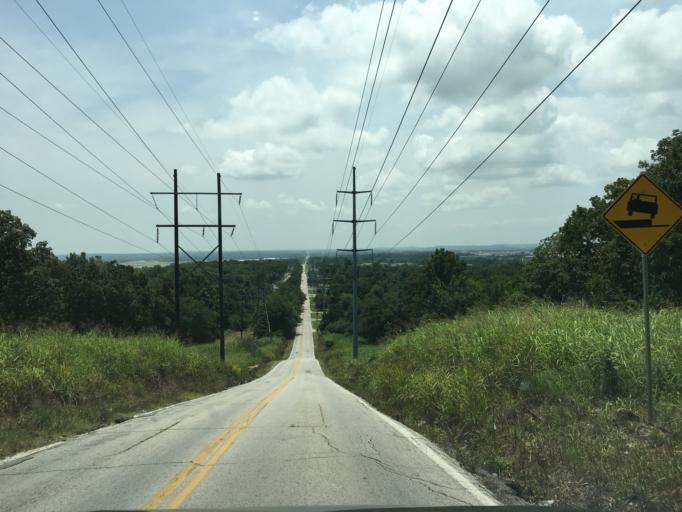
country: US
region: Oklahoma
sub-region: Tulsa County
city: Jenks
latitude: 36.0697
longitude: -95.9939
